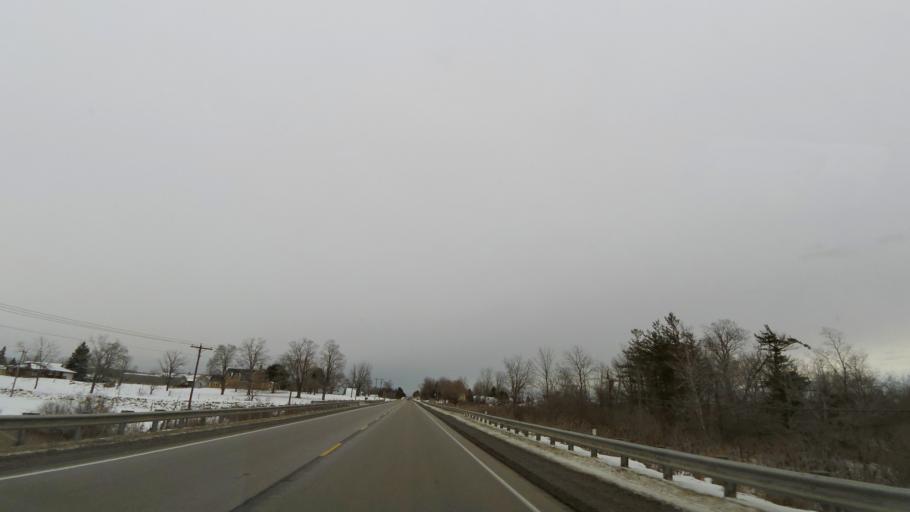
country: CA
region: Ontario
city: Ancaster
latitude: 43.2970
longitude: -79.9742
